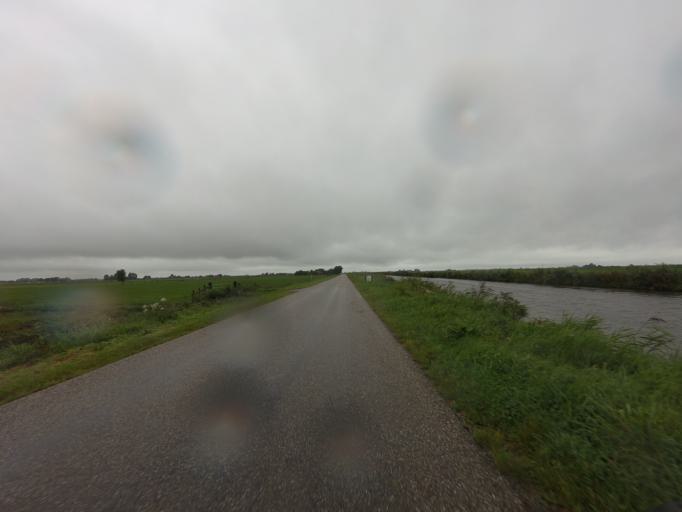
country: NL
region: Friesland
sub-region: Sudwest Fryslan
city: Workum
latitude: 52.9847
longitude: 5.4700
